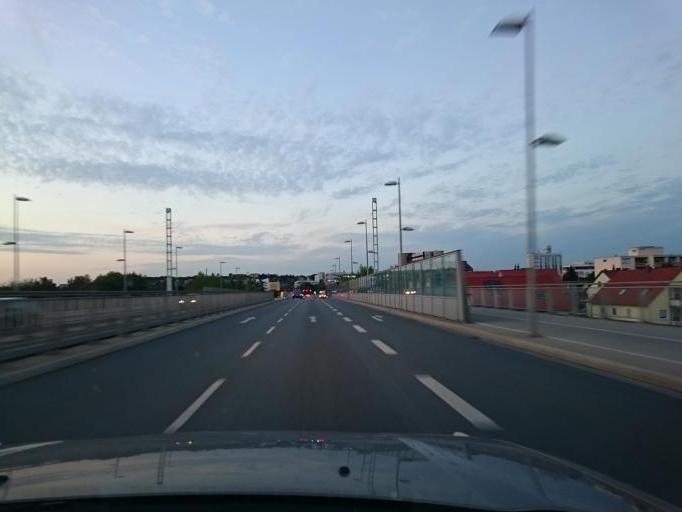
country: DE
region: Bavaria
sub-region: Upper Palatinate
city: Regensburg
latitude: 49.0223
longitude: 12.1134
